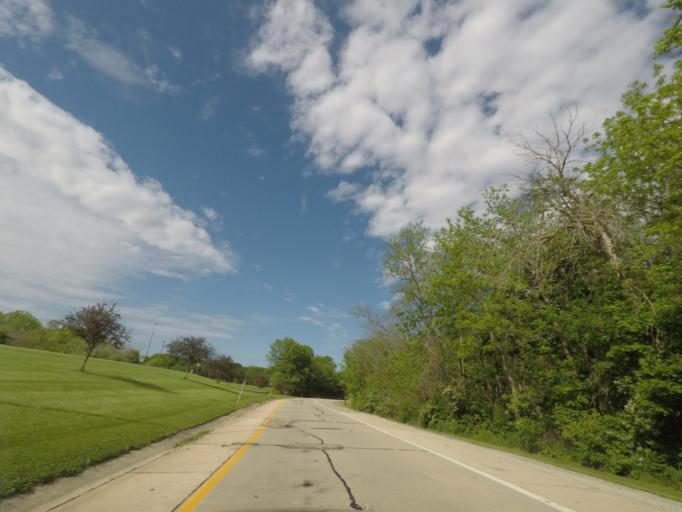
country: US
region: Illinois
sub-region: McLean County
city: Twin Grove
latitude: 40.3626
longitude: -89.1079
